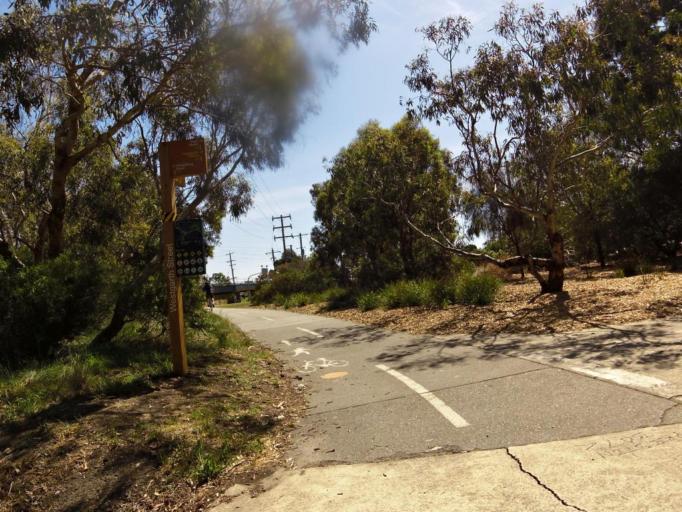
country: AU
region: Victoria
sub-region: Yarra
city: North Fitzroy
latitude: -37.7807
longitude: 144.9924
